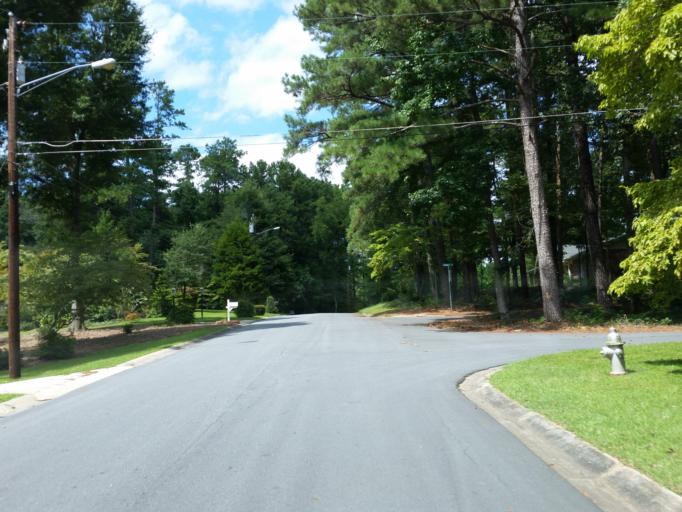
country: US
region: Georgia
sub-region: Cobb County
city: Marietta
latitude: 33.9664
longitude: -84.4857
